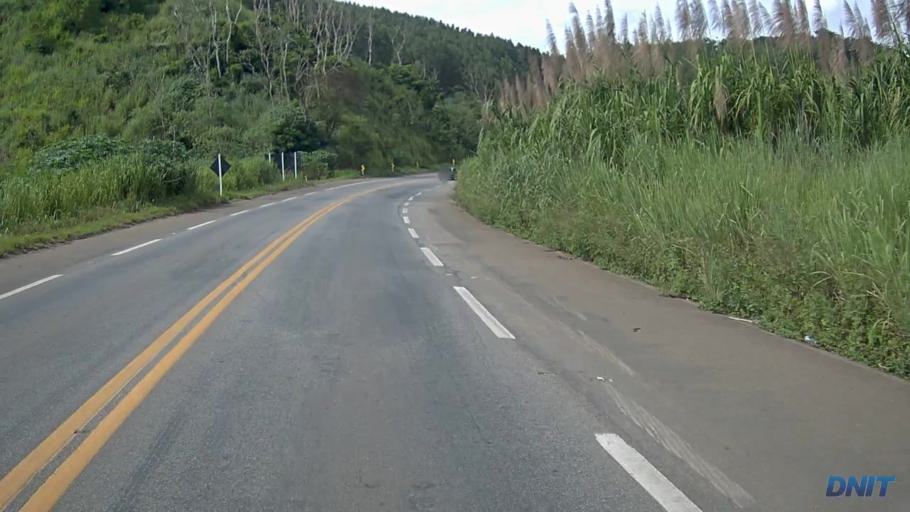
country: BR
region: Minas Gerais
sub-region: Ipaba
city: Ipaba
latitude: -19.3617
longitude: -42.4478
